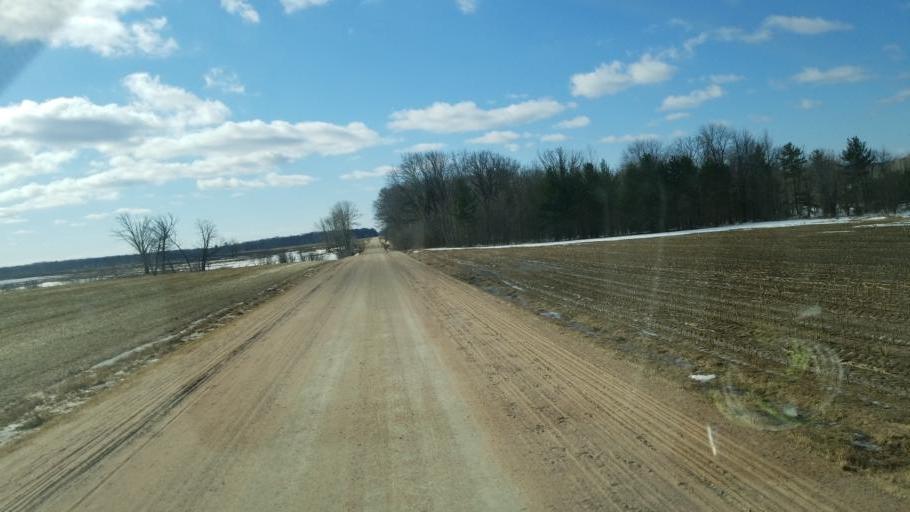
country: US
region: Wisconsin
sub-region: Clark County
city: Loyal
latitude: 44.6327
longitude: -90.3970
